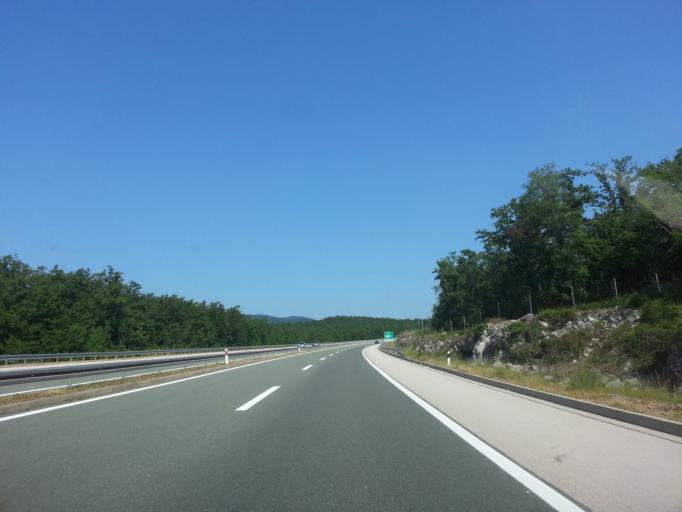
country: HR
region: Primorsko-Goranska
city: Matulji
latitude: 45.4344
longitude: 14.2821
